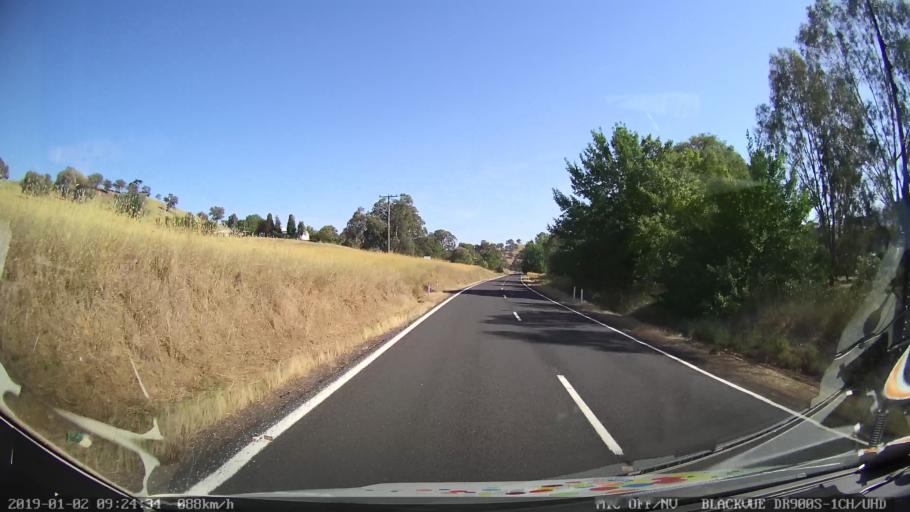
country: AU
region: New South Wales
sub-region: Tumut Shire
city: Tumut
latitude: -35.3754
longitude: 148.2917
